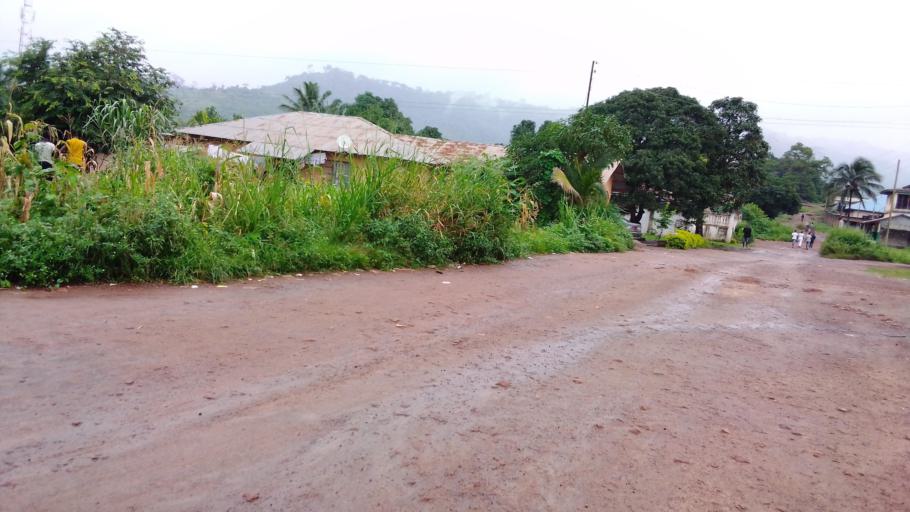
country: SL
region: Eastern Province
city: Kenema
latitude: 7.8971
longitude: -11.1799
